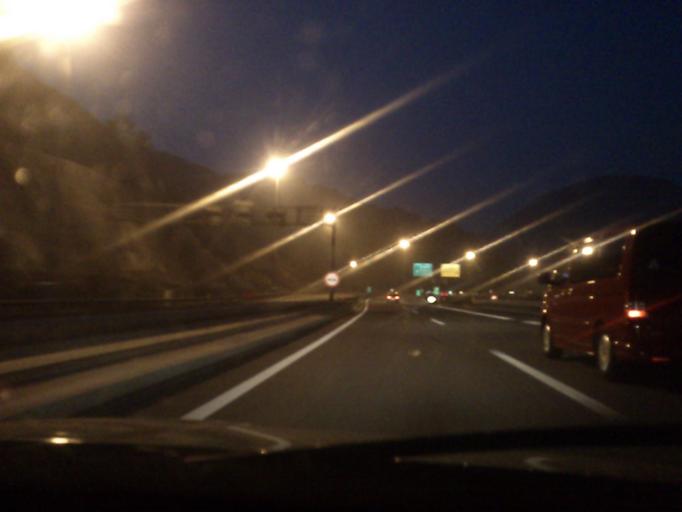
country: HR
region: Krapinsko-Zagorska
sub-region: Grad Krapina
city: Krapina
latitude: 46.2043
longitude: 15.8453
